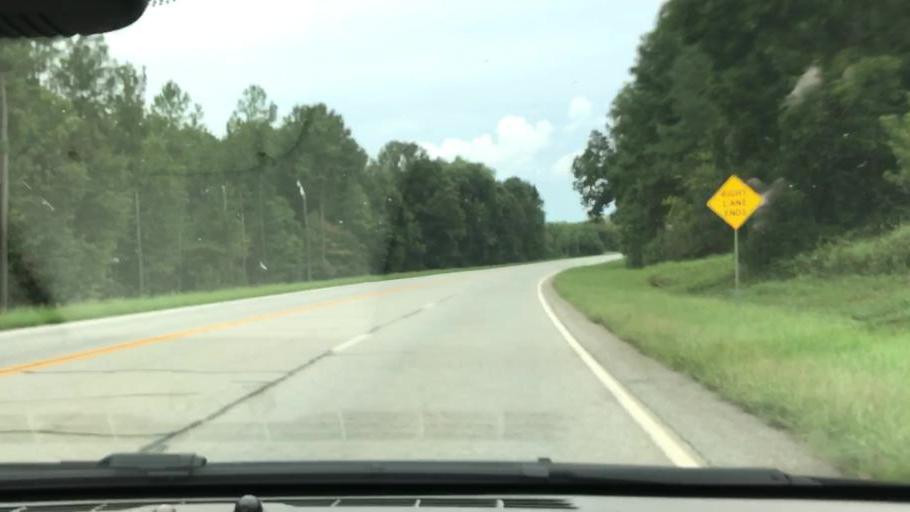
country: US
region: Georgia
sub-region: Early County
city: Blakely
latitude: 31.3326
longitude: -84.9931
